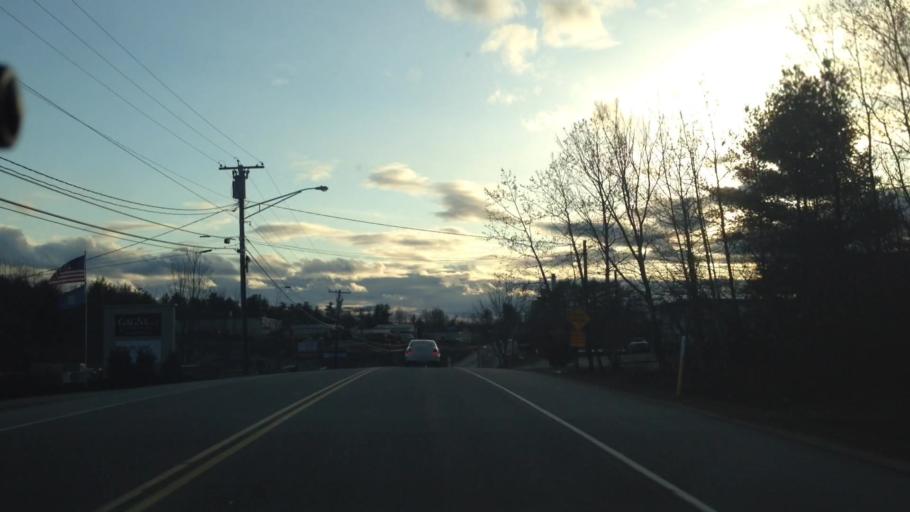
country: US
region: Maine
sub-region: Cumberland County
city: Westbrook
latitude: 43.6859
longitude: -70.3350
